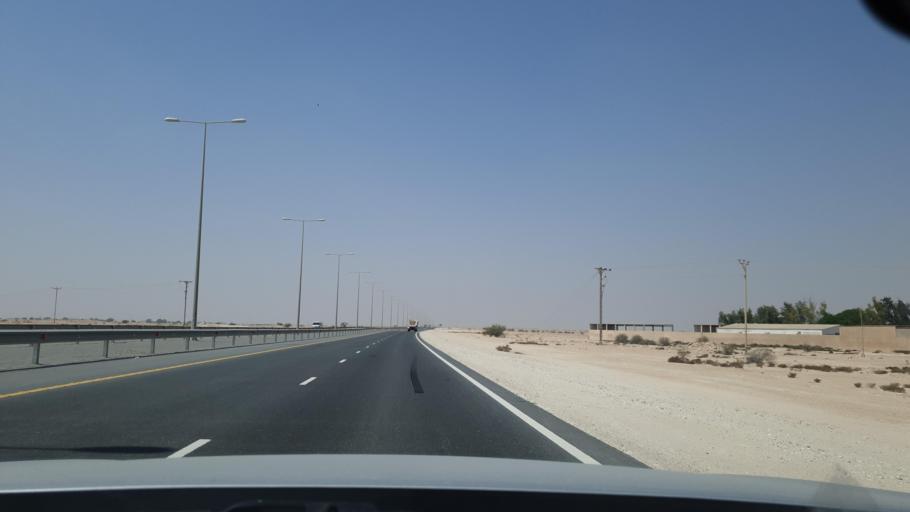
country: QA
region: Baladiyat az Za`ayin
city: Az Za`ayin
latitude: 25.6198
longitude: 51.3518
